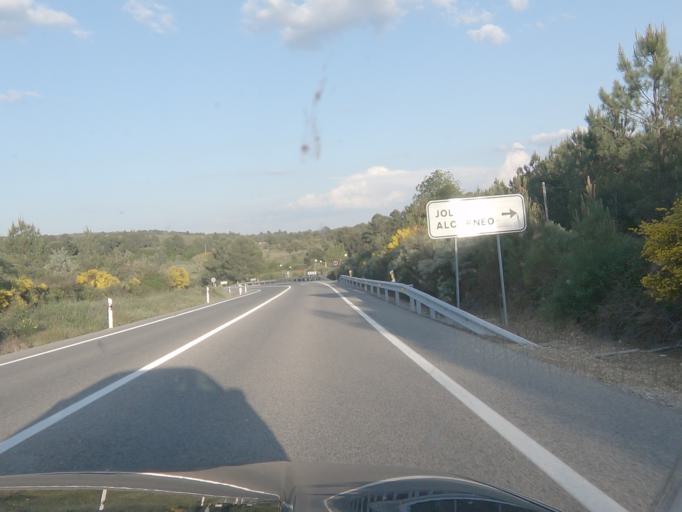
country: PT
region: Portalegre
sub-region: Portalegre
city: Sao Juliao
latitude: 39.3418
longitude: -7.2795
